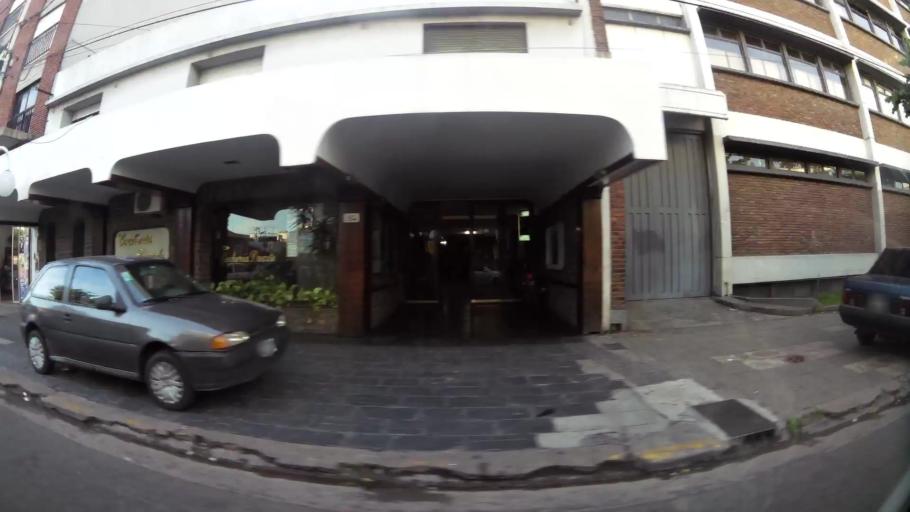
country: AR
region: Buenos Aires
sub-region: Partido de Moron
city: Moron
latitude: -34.6468
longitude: -58.6211
